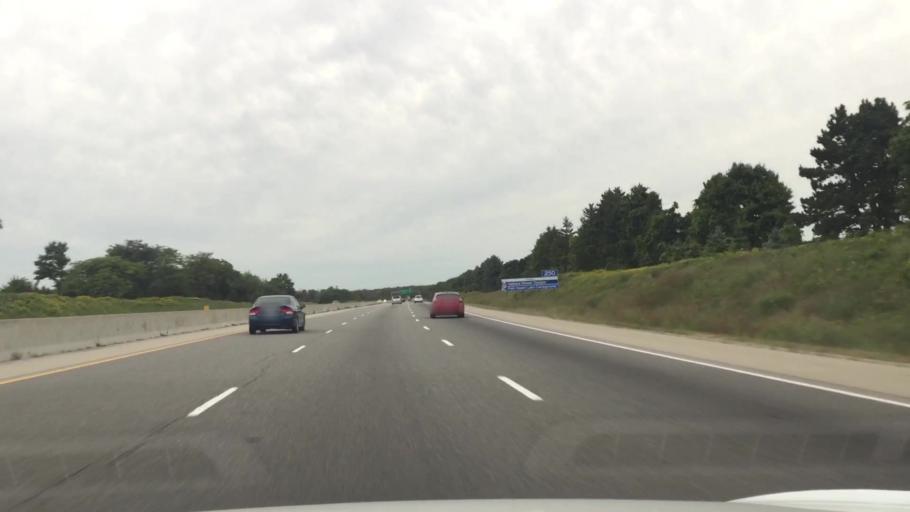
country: CA
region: Ontario
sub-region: Oxford County
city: Woodstock
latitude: 43.2381
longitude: -80.5818
